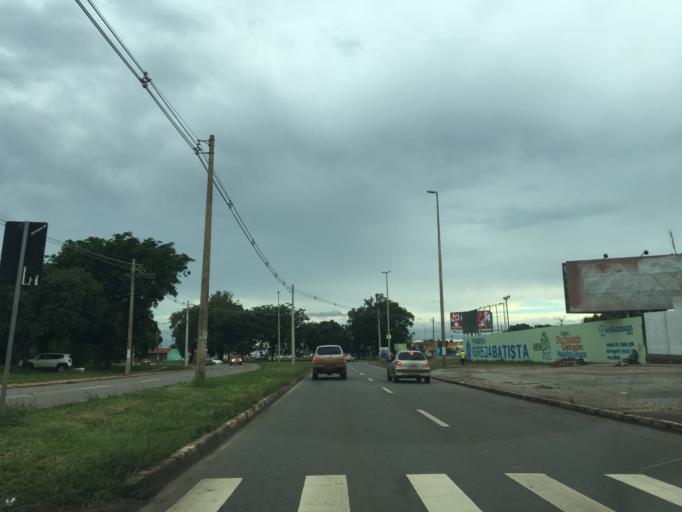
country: BR
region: Goias
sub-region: Luziania
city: Luziania
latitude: -16.0220
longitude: -48.0605
